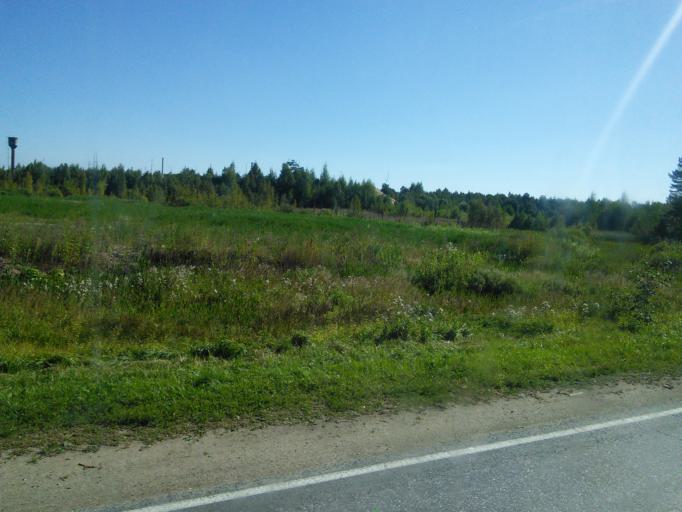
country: RU
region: Jaroslavl
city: Uglich
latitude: 57.4882
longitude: 38.3558
